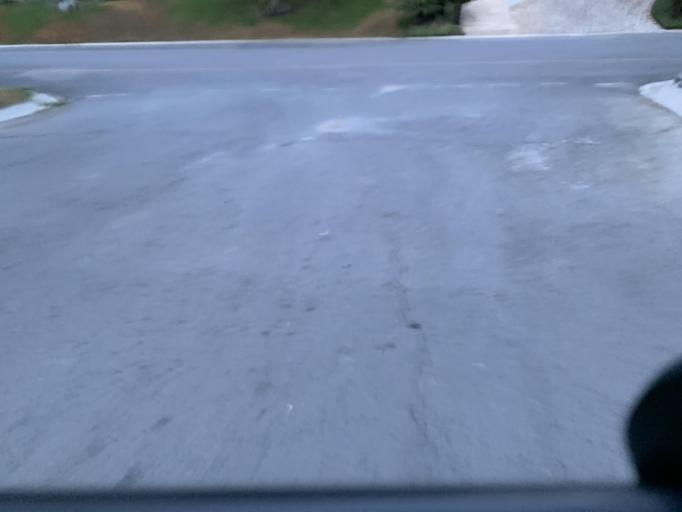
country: MX
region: Nuevo Leon
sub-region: Juarez
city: Bosques de San Pedro
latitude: 25.5154
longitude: -100.1858
